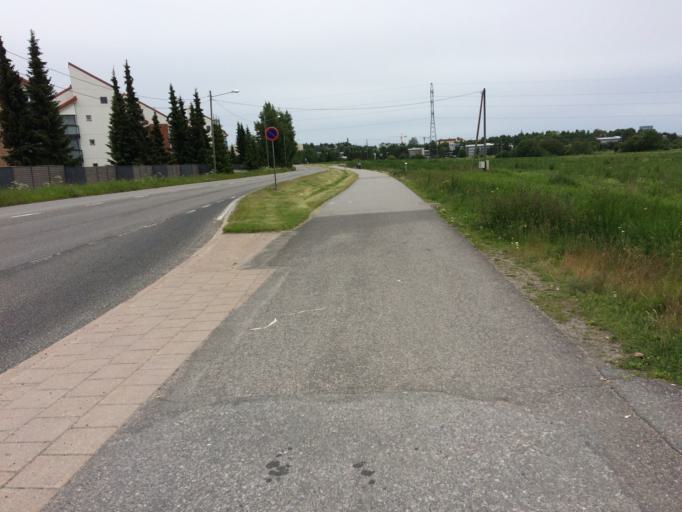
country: FI
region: Varsinais-Suomi
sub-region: Turku
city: Turku
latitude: 60.4691
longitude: 22.3065
